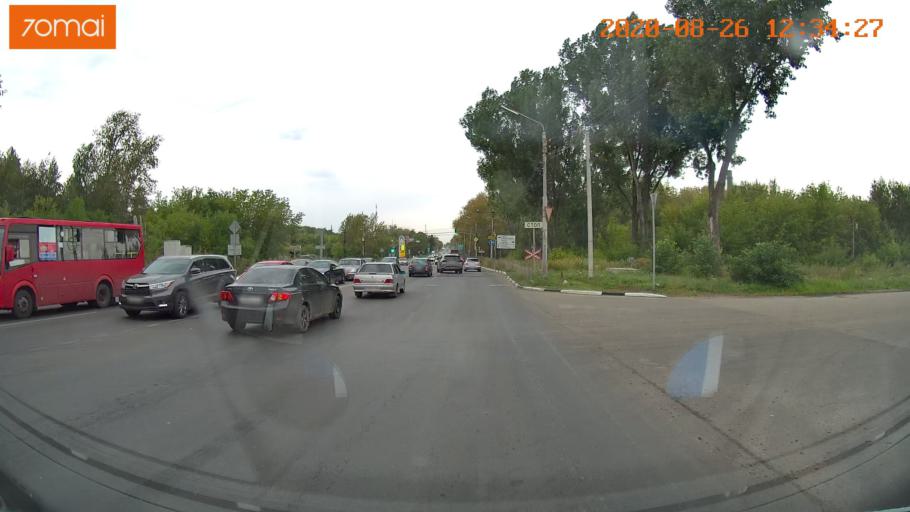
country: RU
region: Rjazan
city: Ryazan'
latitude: 54.5885
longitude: 39.7713
